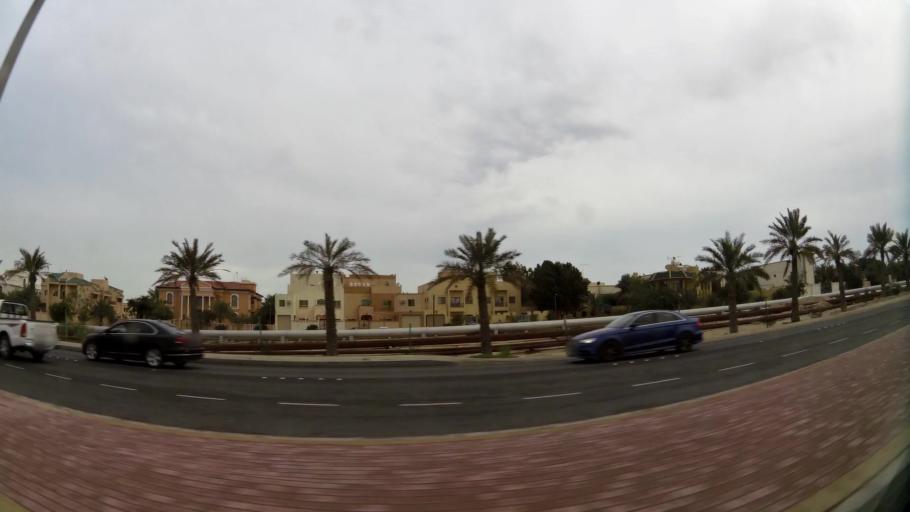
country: BH
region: Central Governorate
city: Madinat Hamad
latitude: 26.1373
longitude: 50.5227
